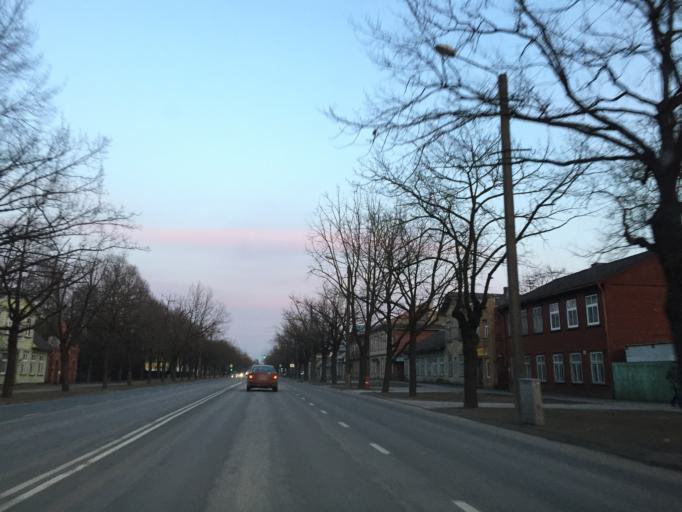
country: EE
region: Paernumaa
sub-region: Paernu linn
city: Parnu
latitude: 58.3809
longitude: 24.5235
